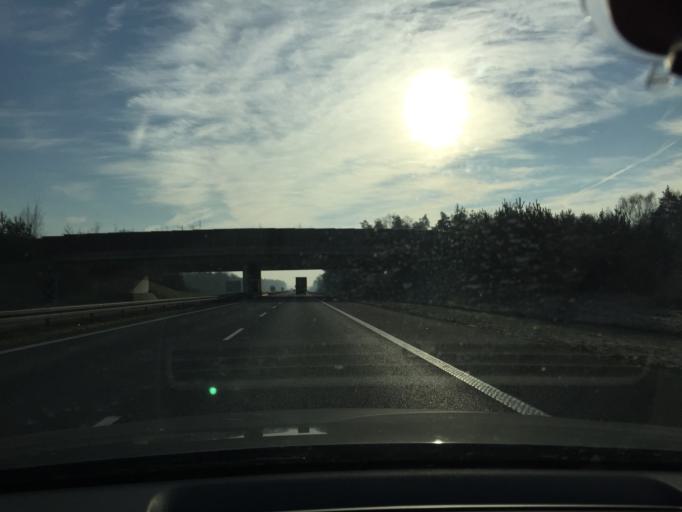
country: PL
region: Silesian Voivodeship
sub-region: Powiat gliwicki
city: Sosnicowice
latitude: 50.3305
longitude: 18.5460
